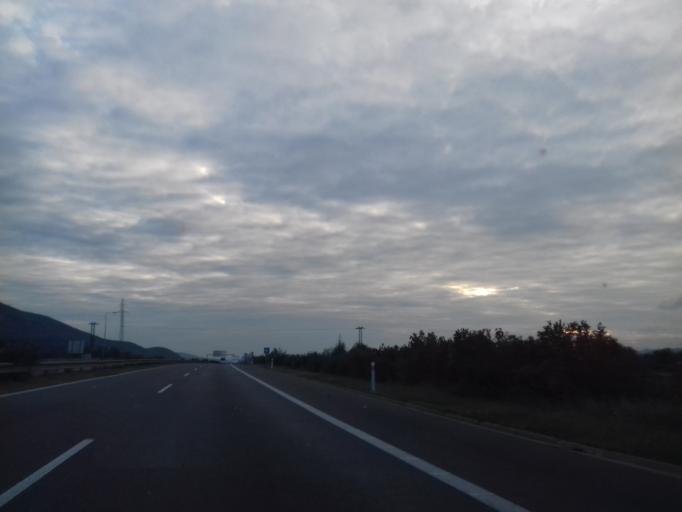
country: SK
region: Nitriansky
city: Puchov
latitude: 49.0536
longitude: 18.3253
